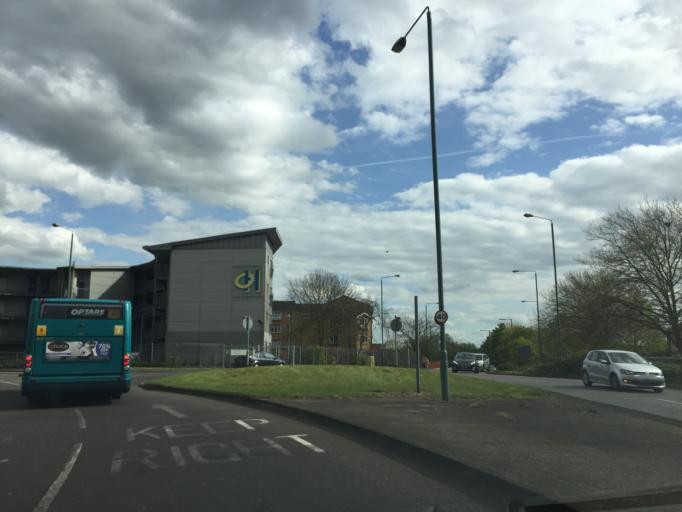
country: GB
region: England
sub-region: Essex
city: Harlow
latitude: 51.7683
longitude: 0.0909
